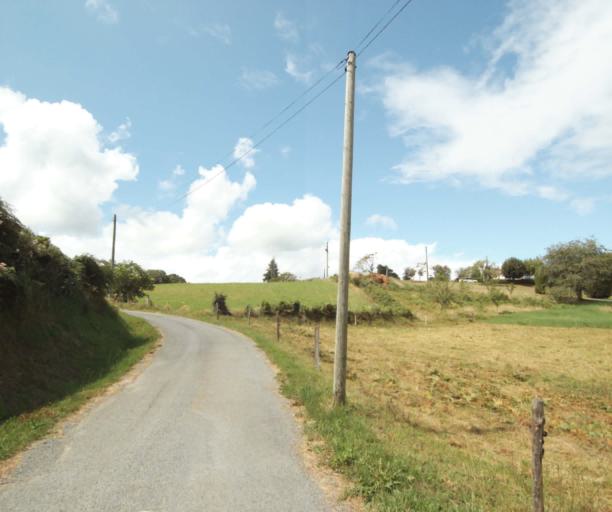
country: FR
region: Limousin
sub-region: Departement de la Correze
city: Sainte-Fortunade
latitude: 45.1782
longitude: 1.8303
